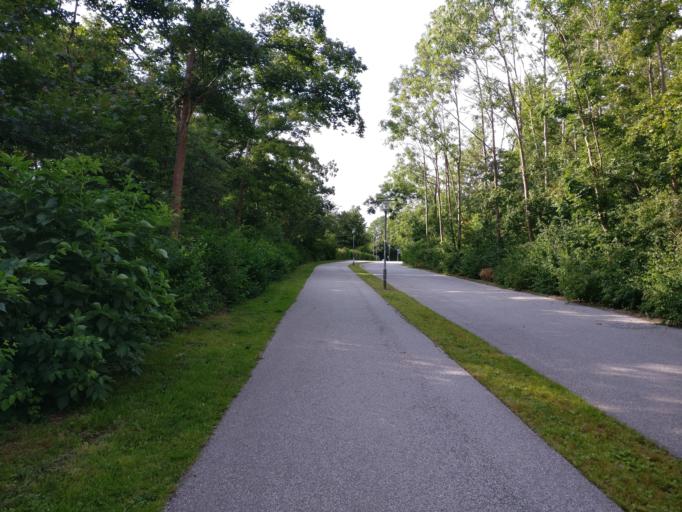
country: DK
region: Capital Region
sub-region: Hvidovre Kommune
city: Hvidovre
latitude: 55.6313
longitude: 12.4538
